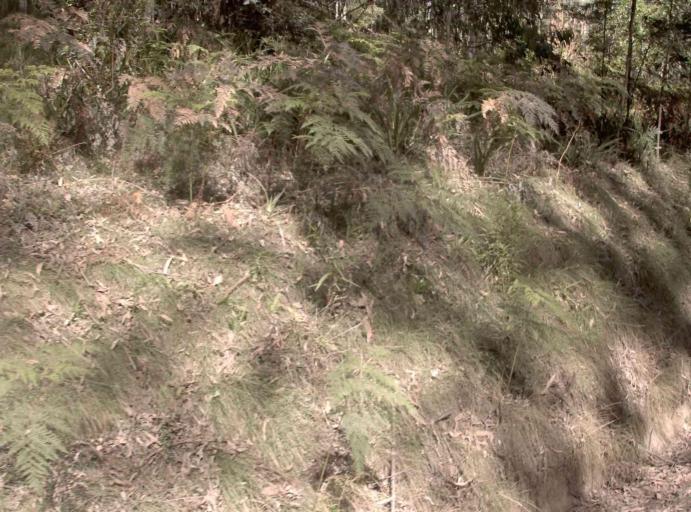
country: AU
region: New South Wales
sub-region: Bombala
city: Bombala
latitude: -37.2265
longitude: 148.7492
